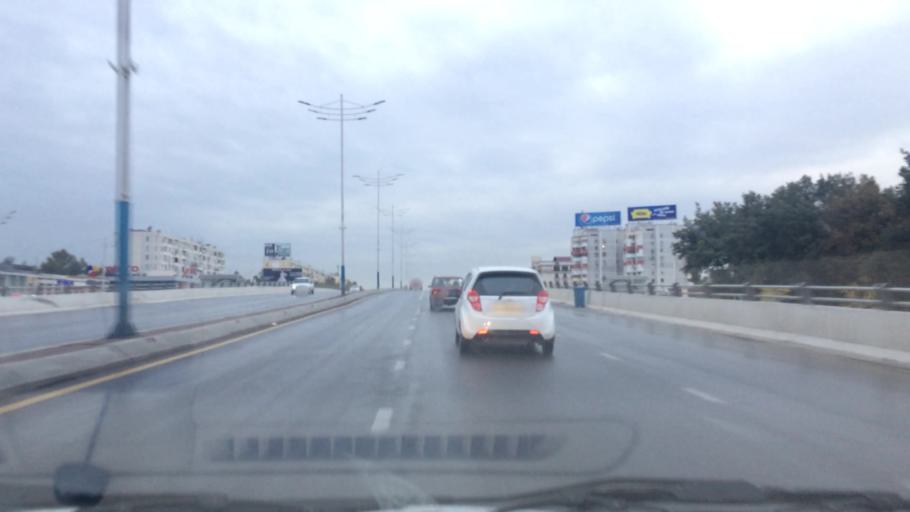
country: UZ
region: Toshkent Shahri
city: Tashkent
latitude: 41.2936
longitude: 69.2250
